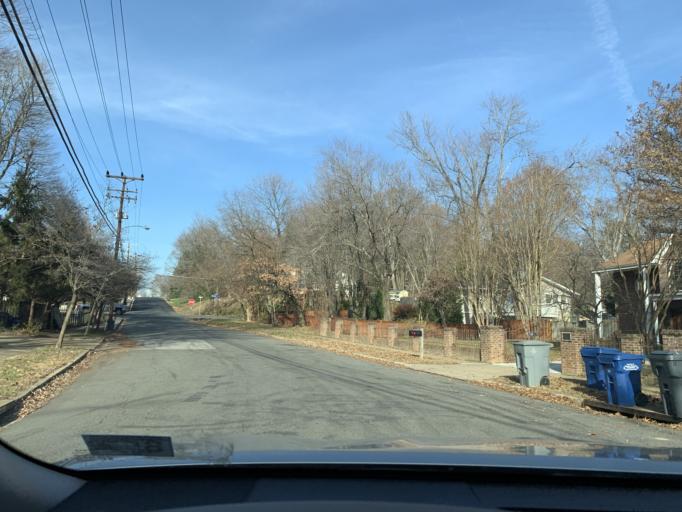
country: US
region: Virginia
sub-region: Fairfax County
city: Jefferson
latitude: 38.8530
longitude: -77.1849
